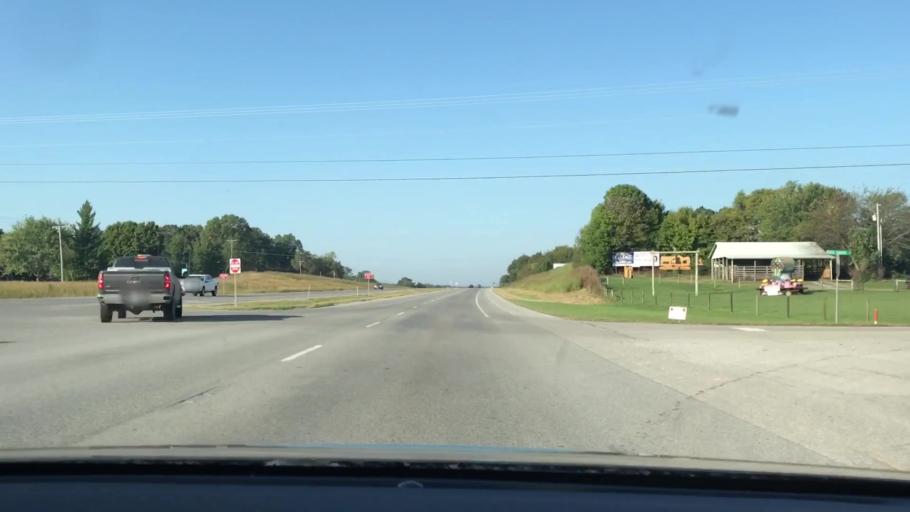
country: US
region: Kentucky
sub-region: Trigg County
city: Cadiz
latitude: 36.8715
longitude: -87.7651
